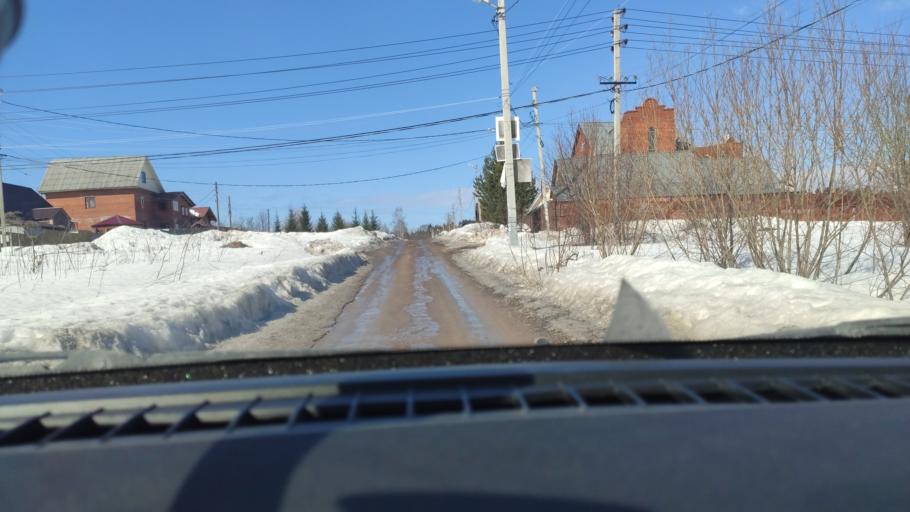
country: RU
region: Perm
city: Perm
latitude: 58.0370
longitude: 56.3957
